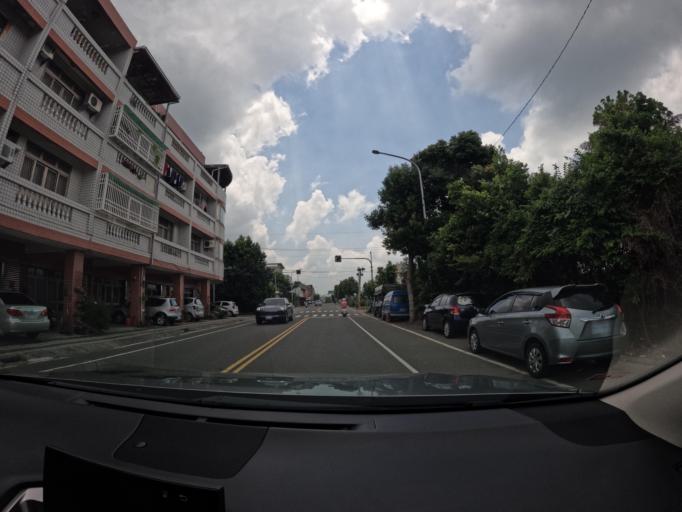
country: TW
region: Taiwan
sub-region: Nantou
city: Nantou
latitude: 23.9110
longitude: 120.6372
